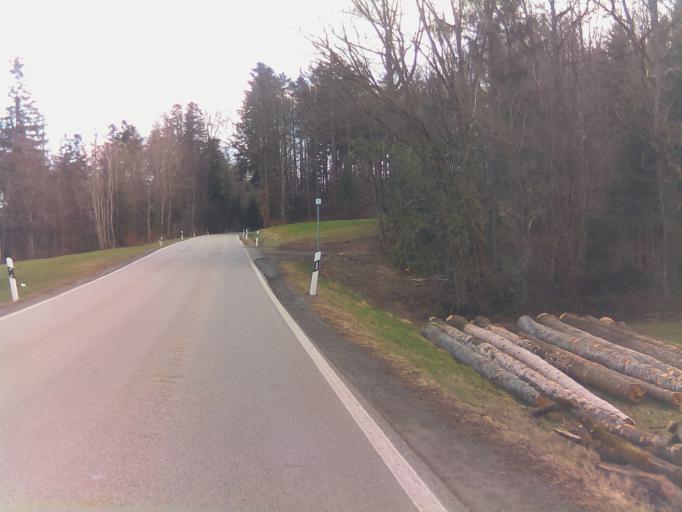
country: DE
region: Baden-Wuerttemberg
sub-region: Regierungsbezirk Stuttgart
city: Grosserlach
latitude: 49.0396
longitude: 9.5429
